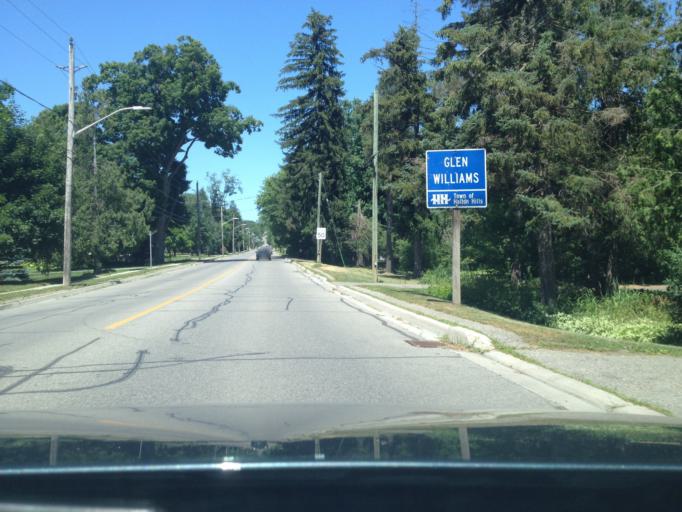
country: CA
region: Ontario
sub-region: Halton
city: Milton
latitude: 43.6634
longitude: -79.9209
